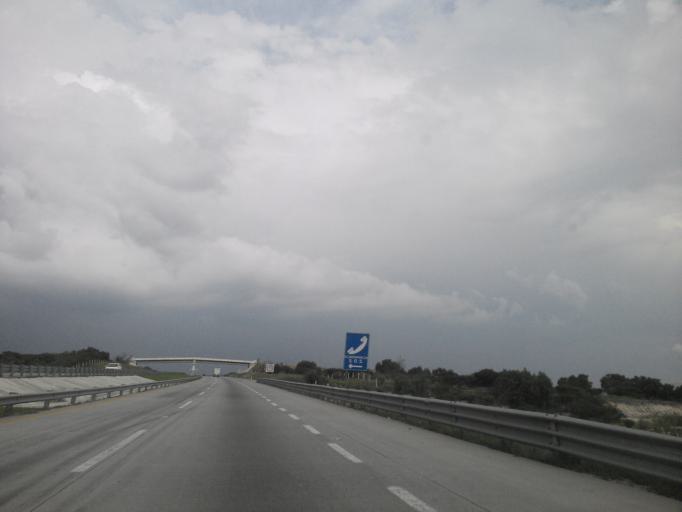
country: MX
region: Mexico
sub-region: Apaxco
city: Colonia Juarez
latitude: 19.9753
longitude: -99.1107
